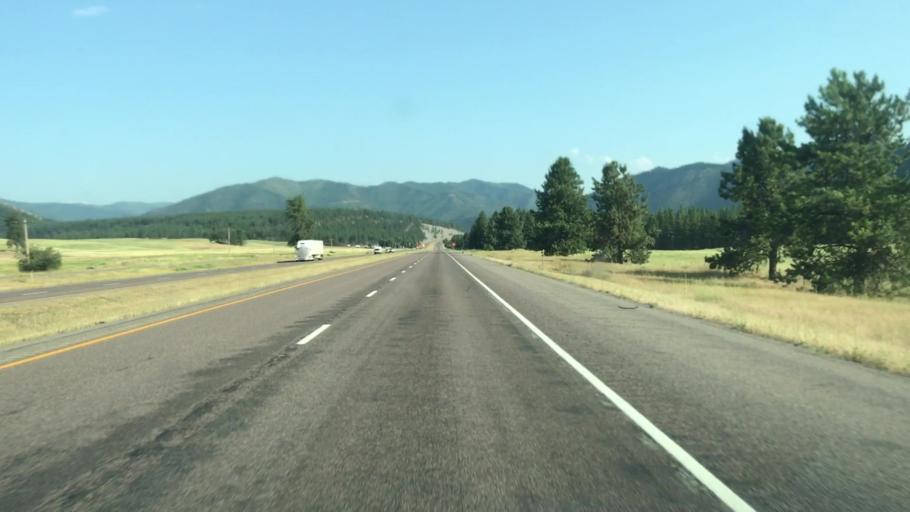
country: US
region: Montana
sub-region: Mineral County
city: Superior
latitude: 47.0403
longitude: -114.7491
